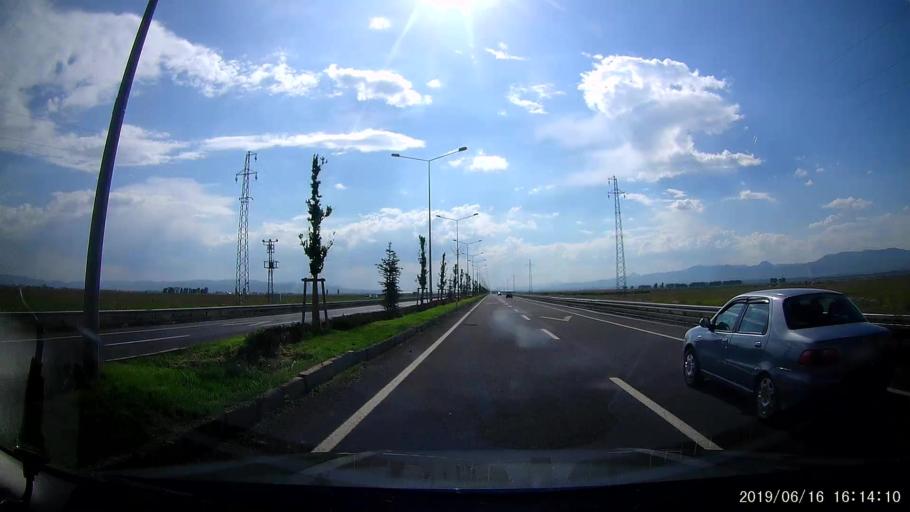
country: TR
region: Erzurum
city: Erzurum
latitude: 39.9601
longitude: 41.2572
